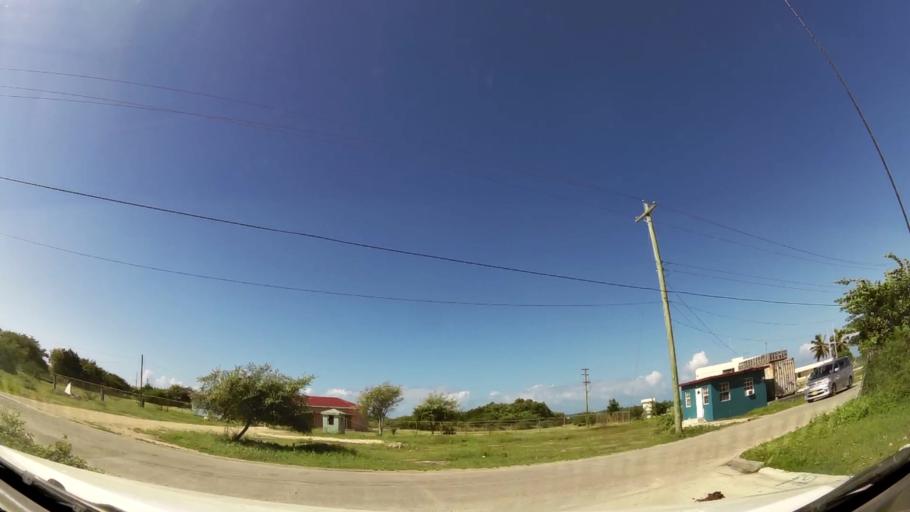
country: AG
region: Barbuda
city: Codrington
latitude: 17.6403
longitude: -61.8277
